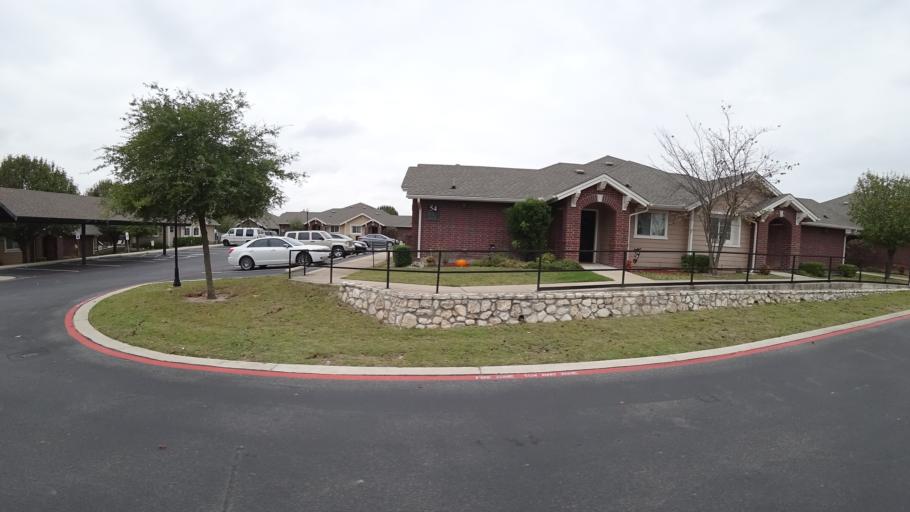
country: US
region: Texas
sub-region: Travis County
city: Pflugerville
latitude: 30.4301
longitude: -97.6213
